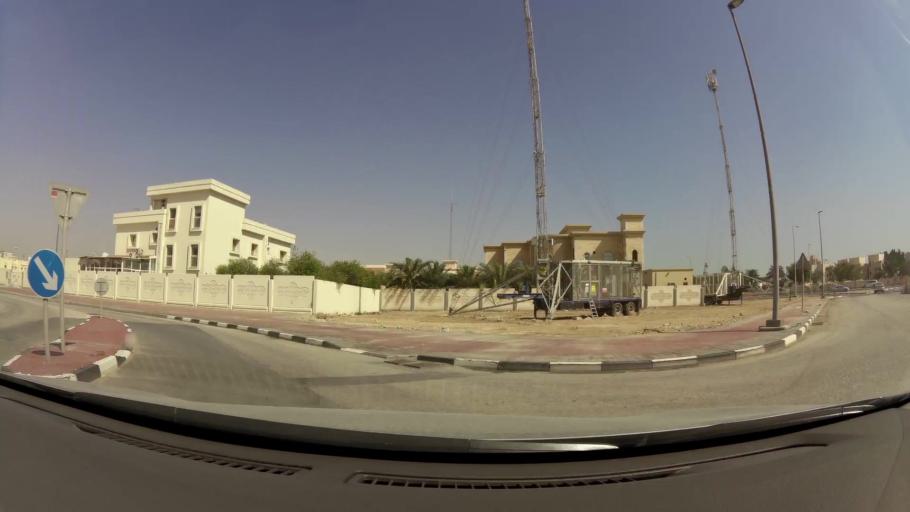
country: QA
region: Baladiyat ad Dawhah
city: Doha
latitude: 25.3624
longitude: 51.5032
